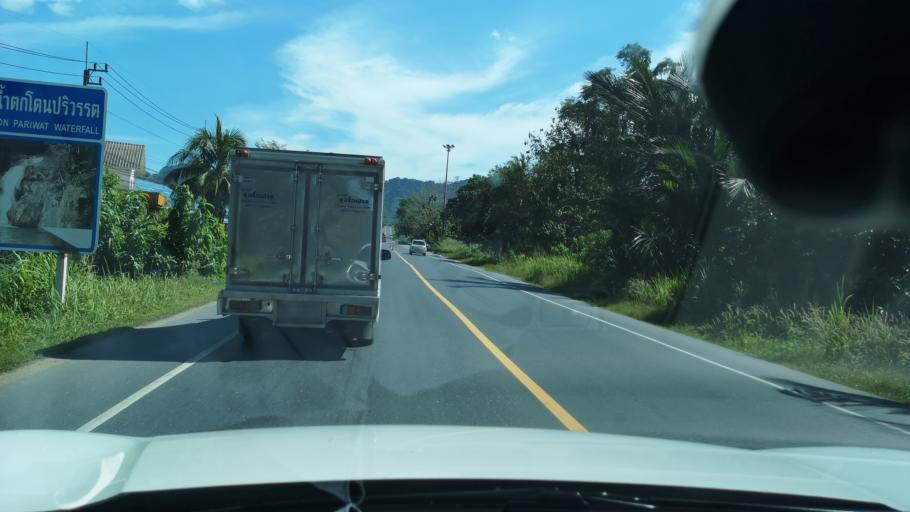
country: TH
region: Phangnga
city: Phang Nga
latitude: 8.5312
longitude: 98.5155
